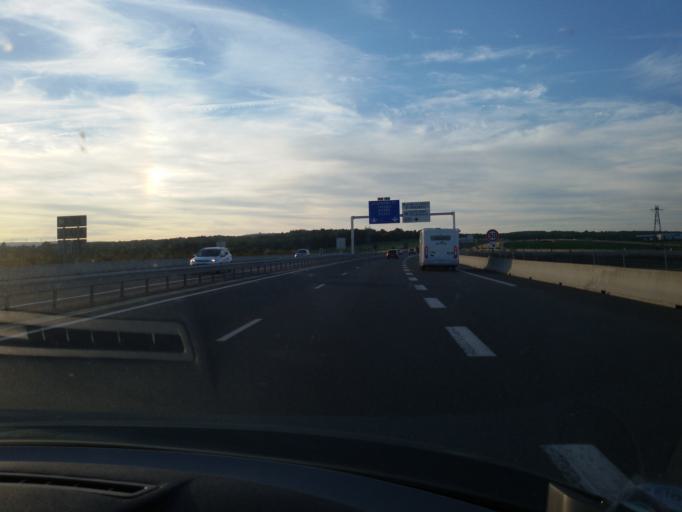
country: FR
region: Midi-Pyrenees
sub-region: Departement de l'Aveyron
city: Creissels
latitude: 44.1364
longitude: 3.0226
